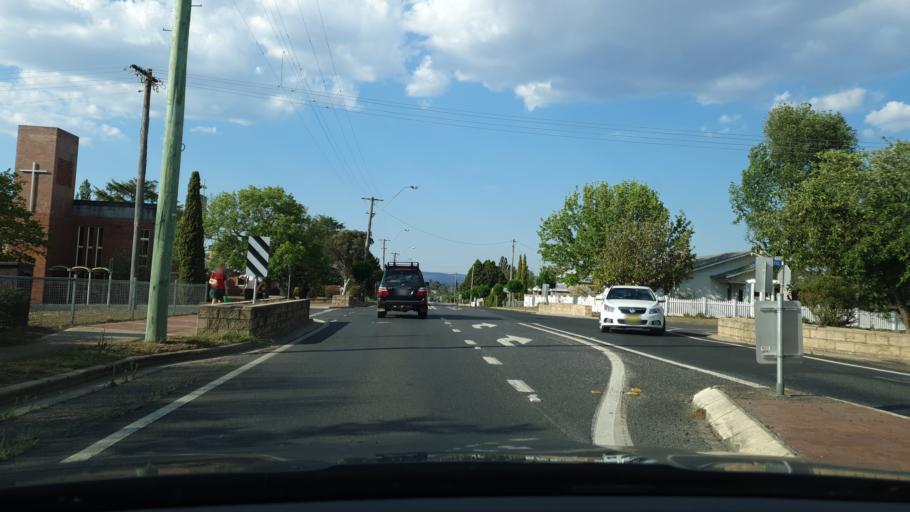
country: AU
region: New South Wales
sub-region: Tenterfield Municipality
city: Carrolls Creek
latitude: -29.0498
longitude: 152.0198
